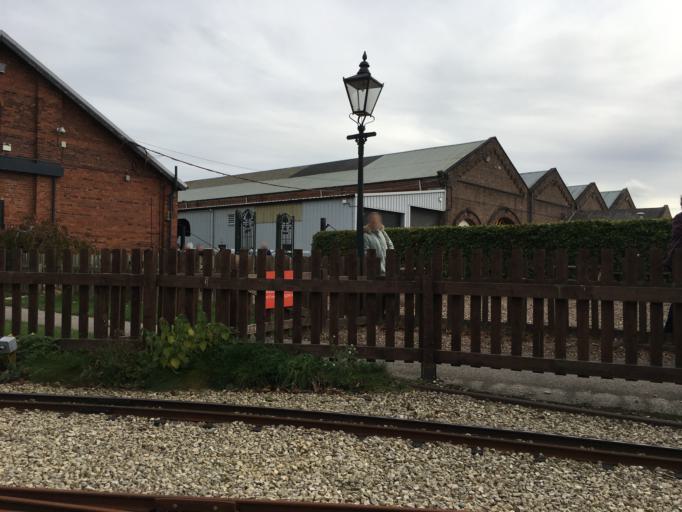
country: GB
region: England
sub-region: City of York
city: York
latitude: 53.9596
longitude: -1.0983
